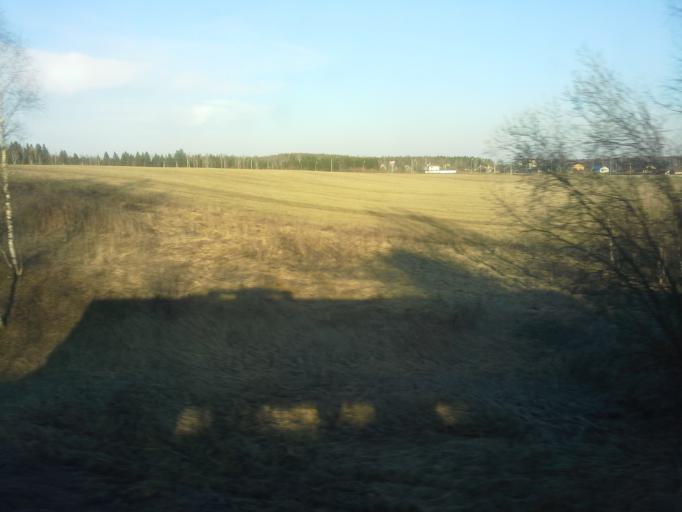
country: RU
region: Moskovskaya
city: Nekrasovskiy
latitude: 56.1073
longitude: 37.5144
